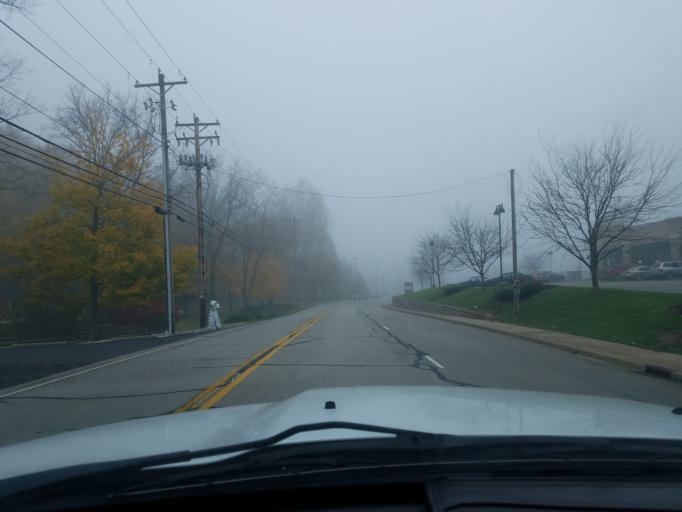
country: US
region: Indiana
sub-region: Floyd County
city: New Albany
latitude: 38.3240
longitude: -85.8705
